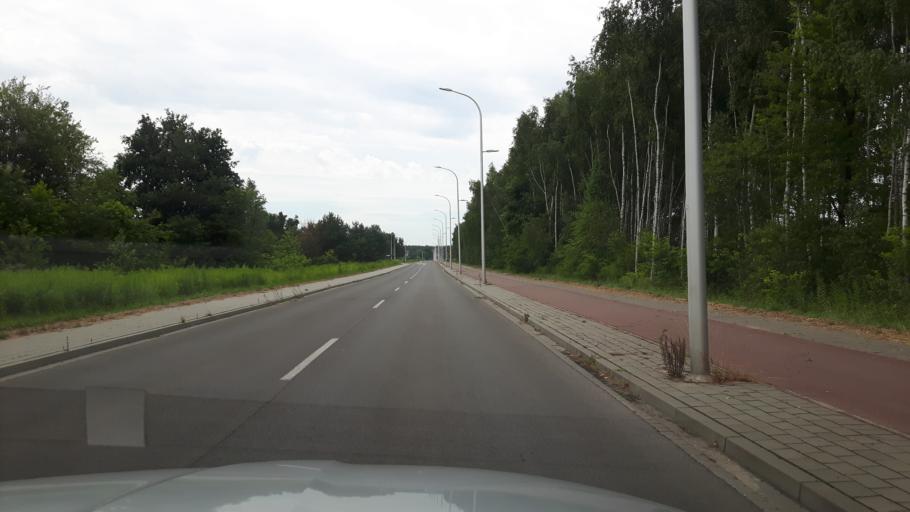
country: PL
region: Masovian Voivodeship
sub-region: Powiat wolominski
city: Wolomin
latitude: 52.3176
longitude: 21.2205
